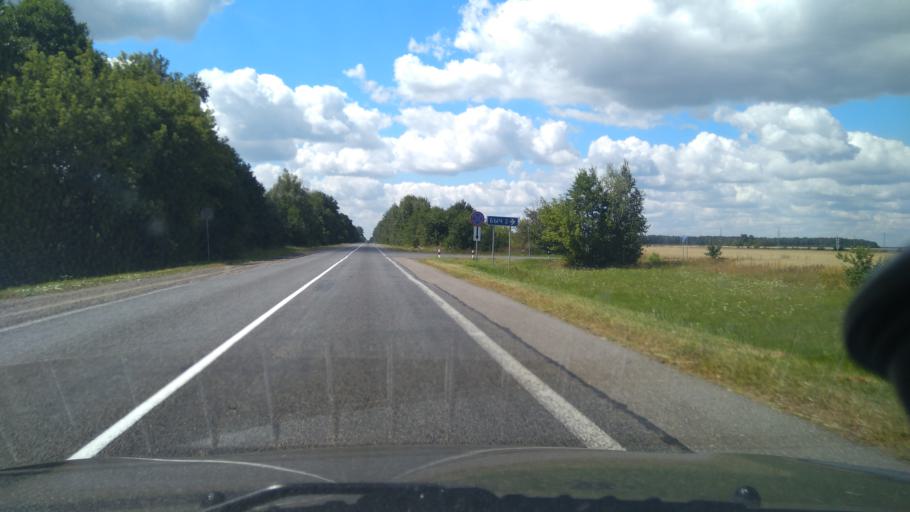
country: BY
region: Brest
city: Ivatsevichy
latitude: 52.6825
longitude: 25.2834
